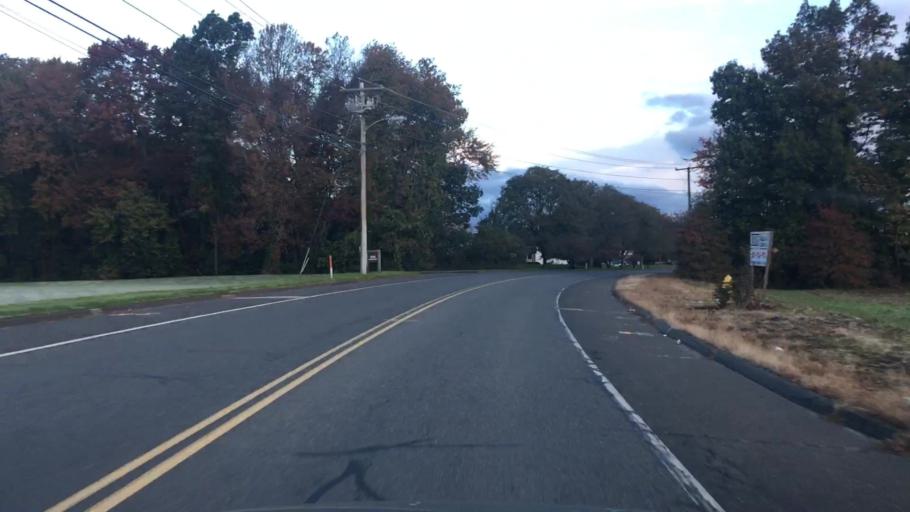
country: US
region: Massachusetts
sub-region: Hampden County
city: East Longmeadow
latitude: 42.0426
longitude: -72.5315
